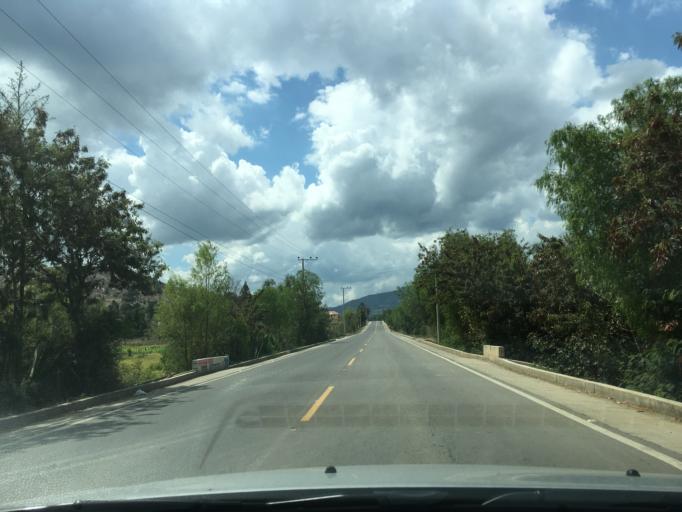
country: CO
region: Boyaca
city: Sutamarchan
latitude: 5.6228
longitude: -73.5980
